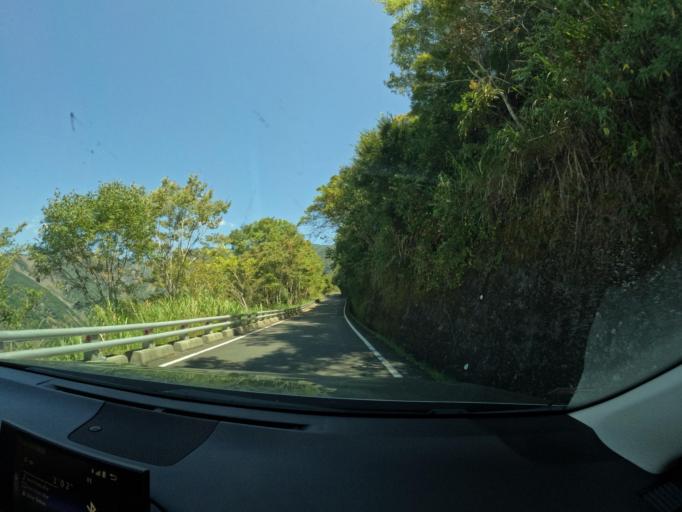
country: TW
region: Taiwan
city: Yujing
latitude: 23.2879
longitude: 120.8500
